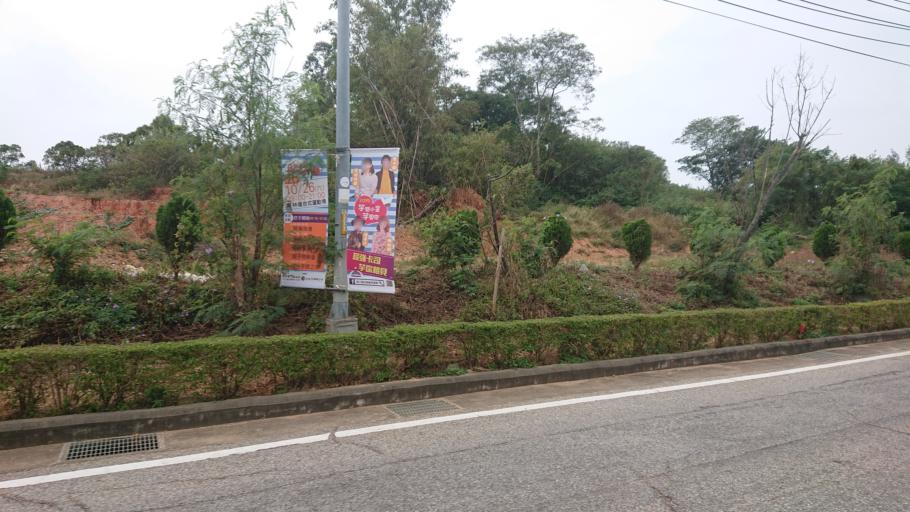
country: TW
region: Fukien
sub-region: Kinmen
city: Jincheng
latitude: 24.4286
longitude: 118.2509
